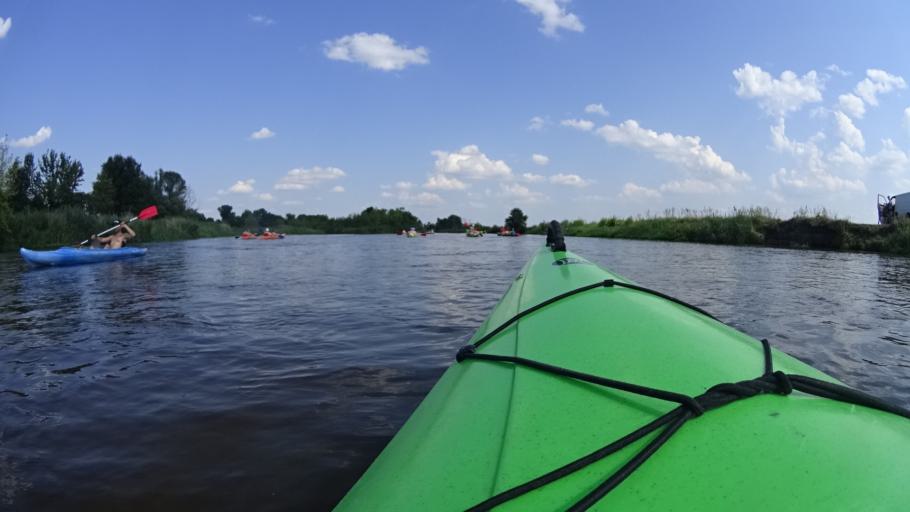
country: PL
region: Masovian Voivodeship
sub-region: Powiat bialobrzeski
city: Wysmierzyce
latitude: 51.6617
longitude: 20.8689
